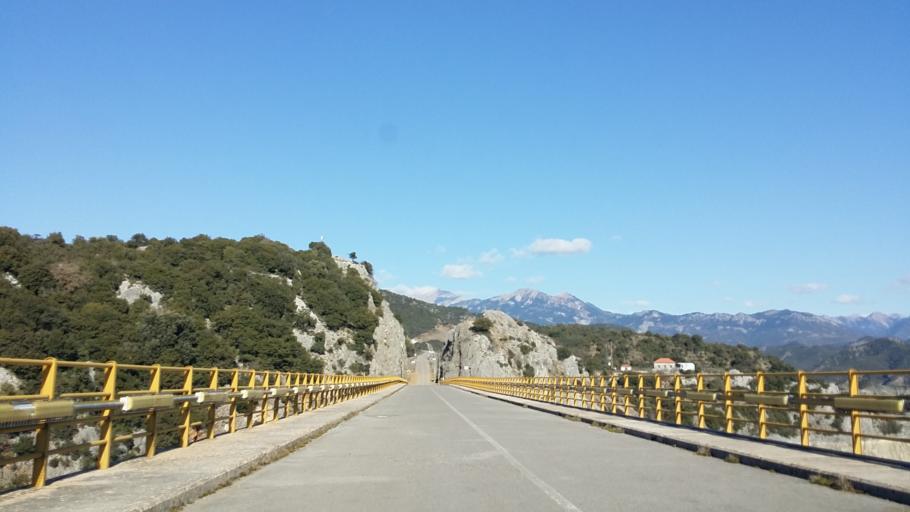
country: GR
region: Central Greece
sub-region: Nomos Evrytanias
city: Kerasochori
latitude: 38.9708
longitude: 21.4914
